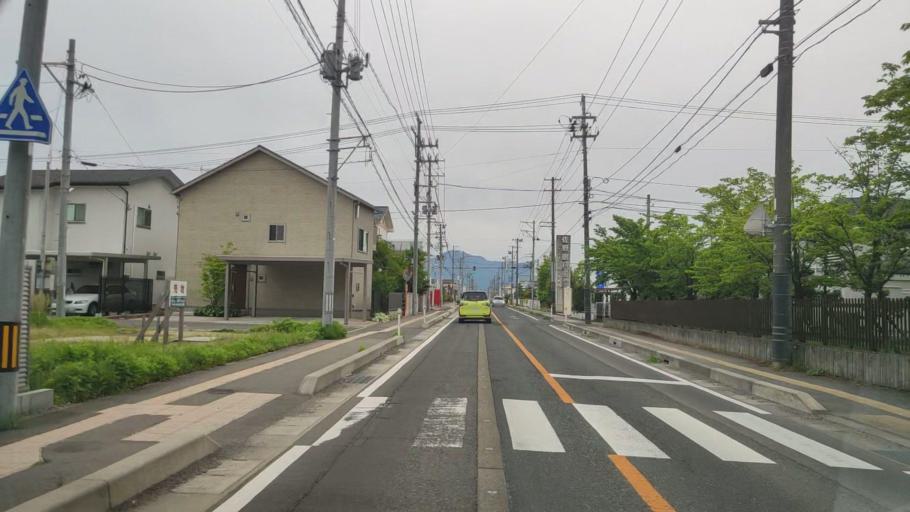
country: JP
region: Niigata
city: Gosen
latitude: 37.7343
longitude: 139.1766
